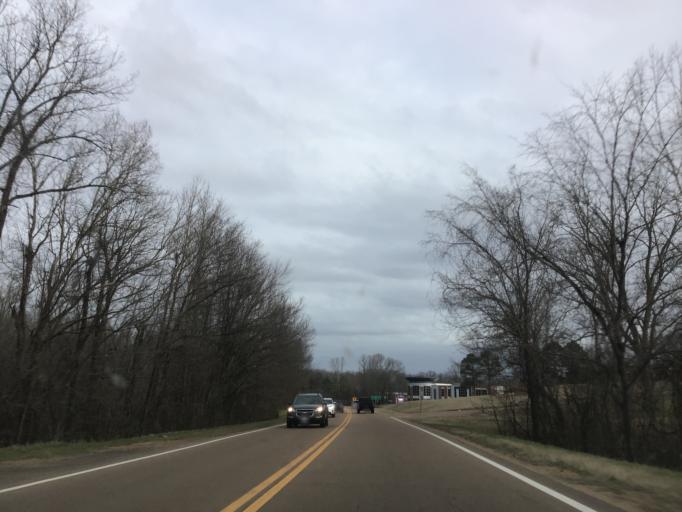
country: US
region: Mississippi
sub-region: Warren County
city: Beechwood
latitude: 32.3363
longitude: -90.8251
